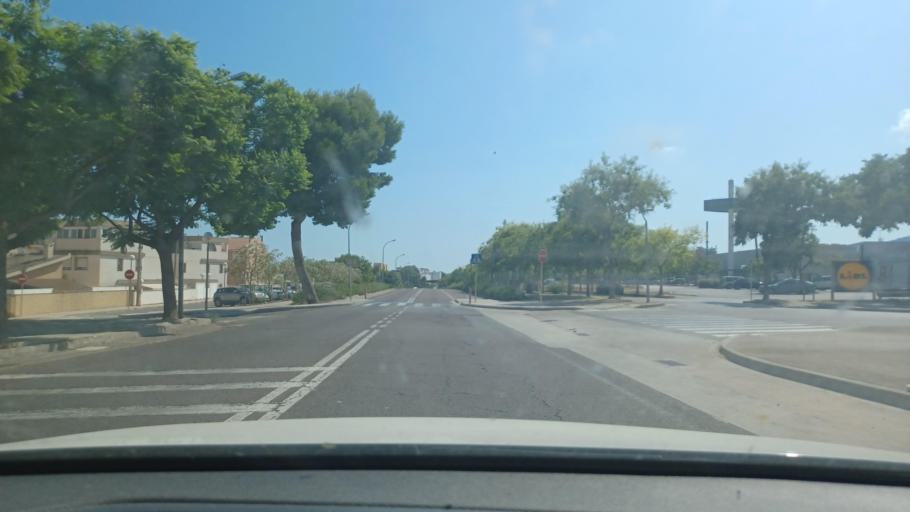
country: ES
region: Catalonia
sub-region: Provincia de Tarragona
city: Sant Carles de la Rapita
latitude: 40.6110
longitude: 0.5850
